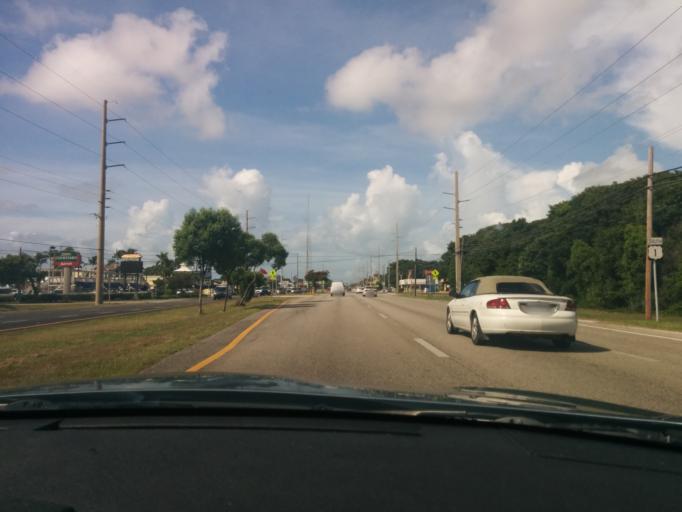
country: US
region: Florida
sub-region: Monroe County
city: Key Largo
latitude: 25.0974
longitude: -80.4376
